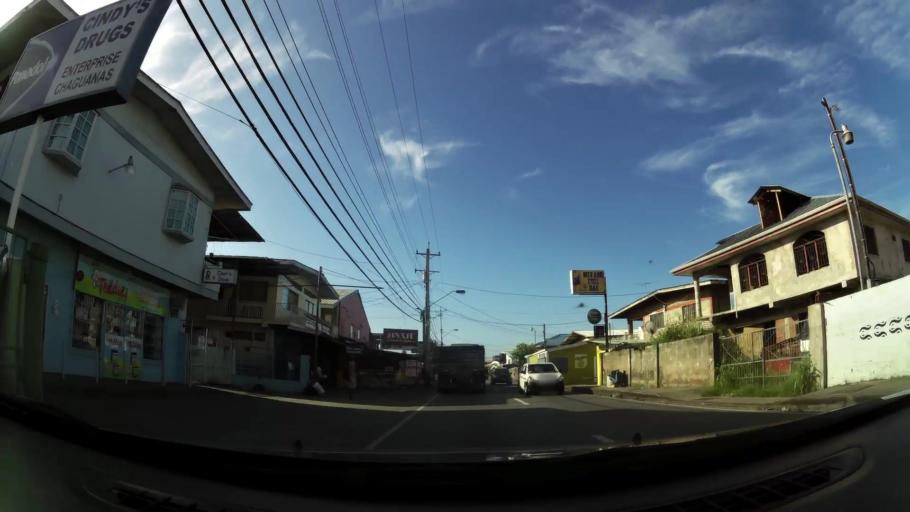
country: TT
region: Chaguanas
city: Chaguanas
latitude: 10.5331
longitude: -61.3811
